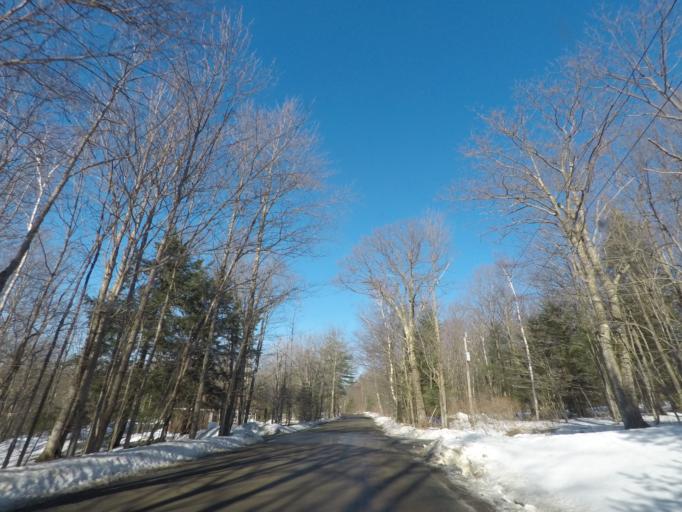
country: US
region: New York
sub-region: Rensselaer County
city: Averill Park
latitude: 42.6425
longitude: -73.5026
